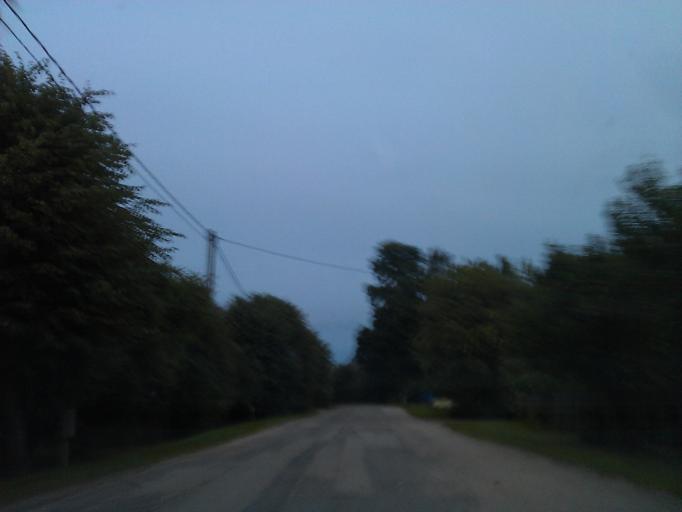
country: LV
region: Sigulda
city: Sigulda
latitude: 57.1476
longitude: 24.8431
